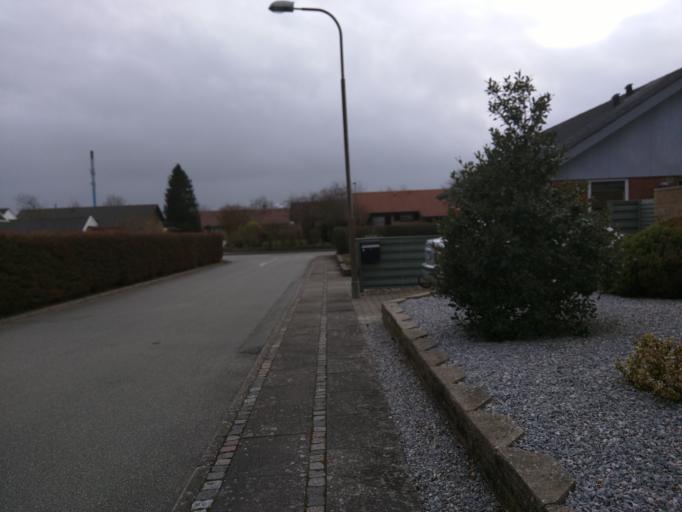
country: DK
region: South Denmark
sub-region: Fredericia Kommune
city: Snoghoj
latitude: 55.5394
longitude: 9.7133
